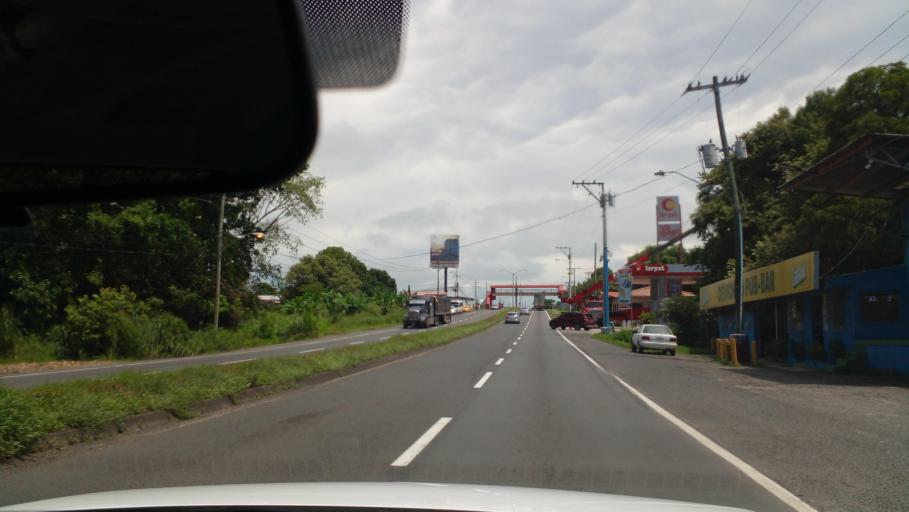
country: PA
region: Panama
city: Nueva Gorgona
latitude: 8.4763
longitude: -79.9593
